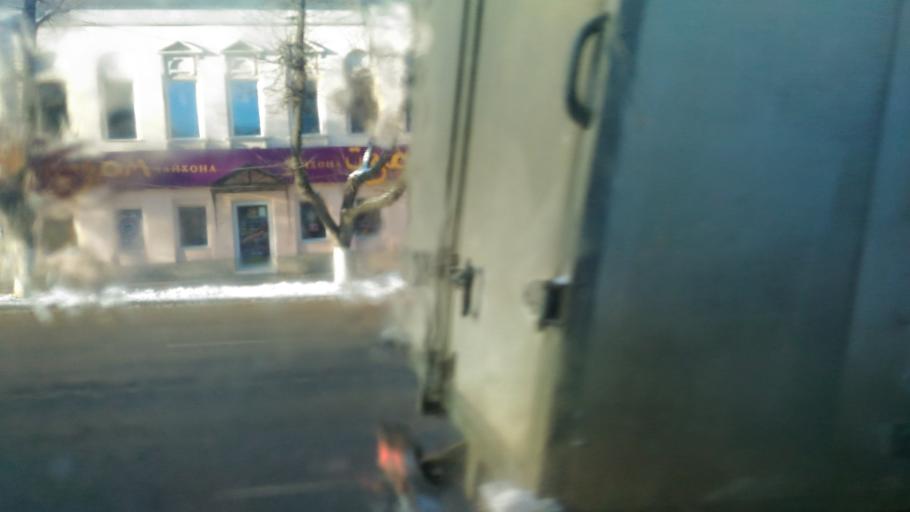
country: RU
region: Tula
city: Tula
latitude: 54.1883
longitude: 37.6122
